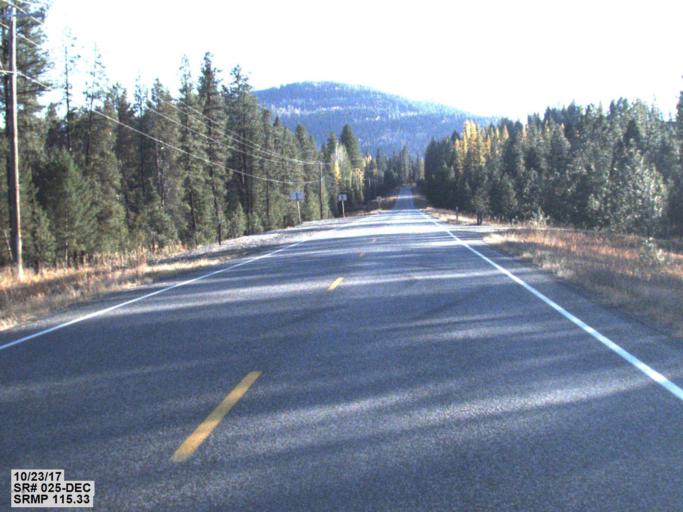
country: CA
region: British Columbia
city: Rossland
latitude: 48.9394
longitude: -117.7723
